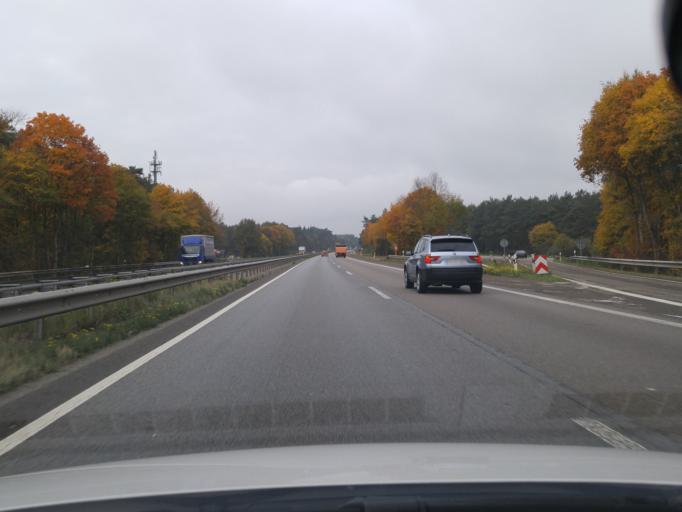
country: DE
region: Rheinland-Pfalz
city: Schifferstadt
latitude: 49.3554
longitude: 8.3864
